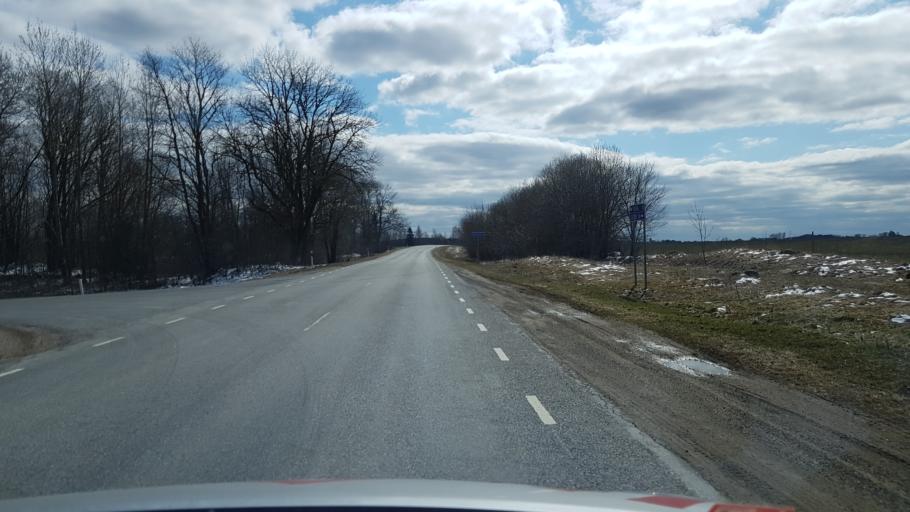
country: EE
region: Laeaene-Virumaa
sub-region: Tapa vald
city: Tapa
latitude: 59.3252
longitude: 26.0027
